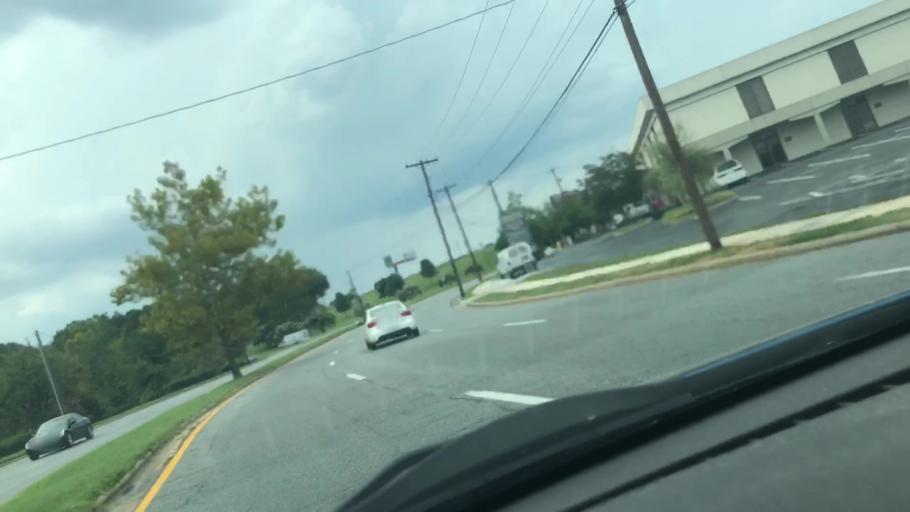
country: US
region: North Carolina
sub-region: Guilford County
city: Greensboro
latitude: 36.0862
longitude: -79.8069
